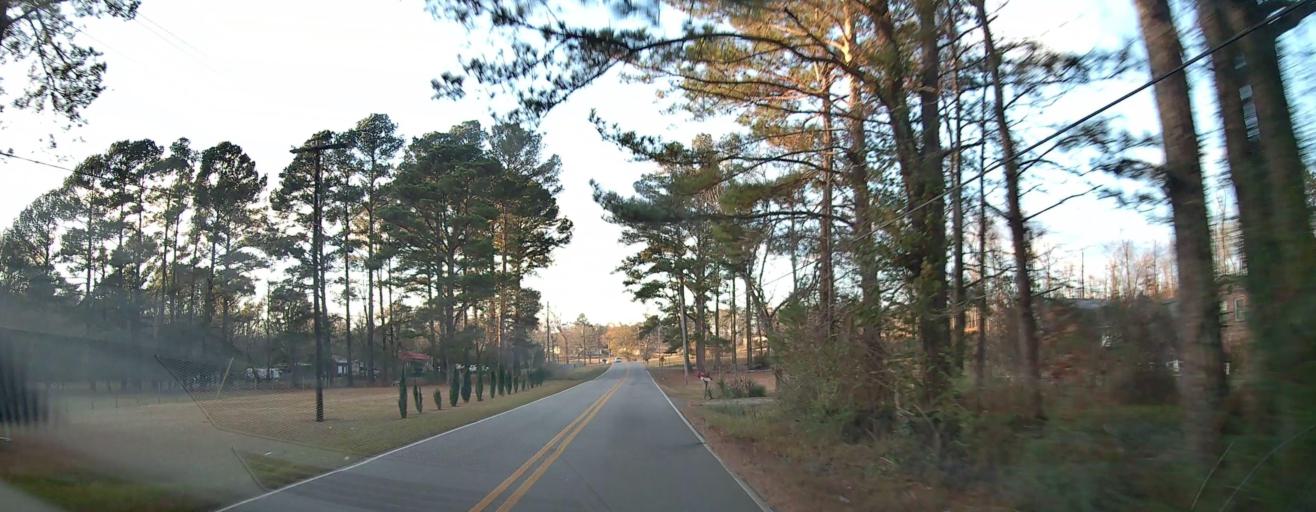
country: US
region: Alabama
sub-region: Etowah County
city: Gadsden
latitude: 33.9763
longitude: -85.9797
